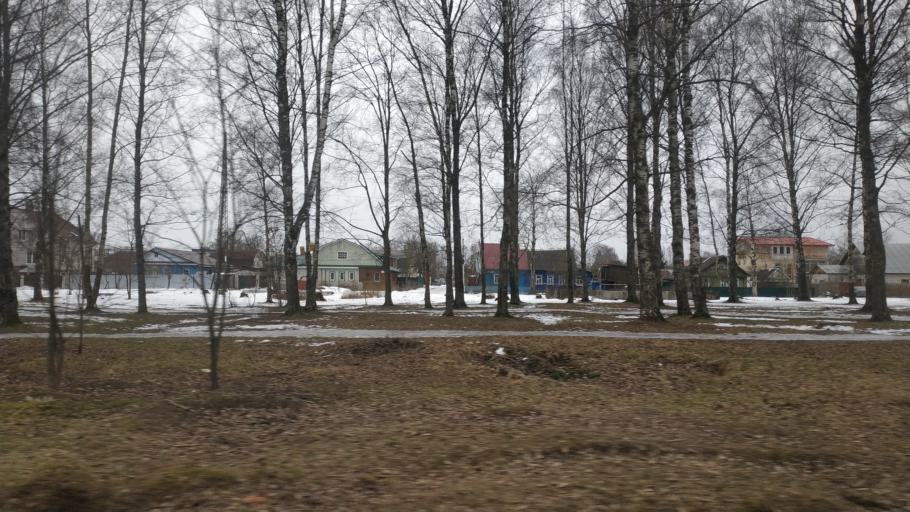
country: RU
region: Tverskaya
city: Tver
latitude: 56.8832
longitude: 35.8905
